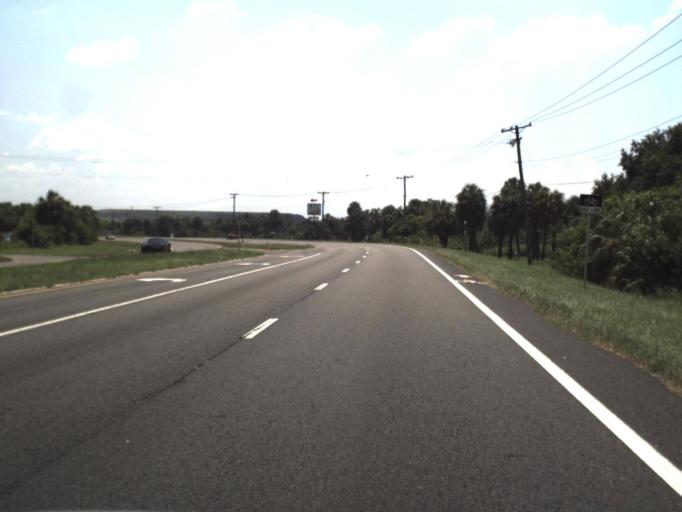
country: US
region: Florida
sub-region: Hillsborough County
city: Palm River-Clair Mel
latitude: 27.8945
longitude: -82.4020
